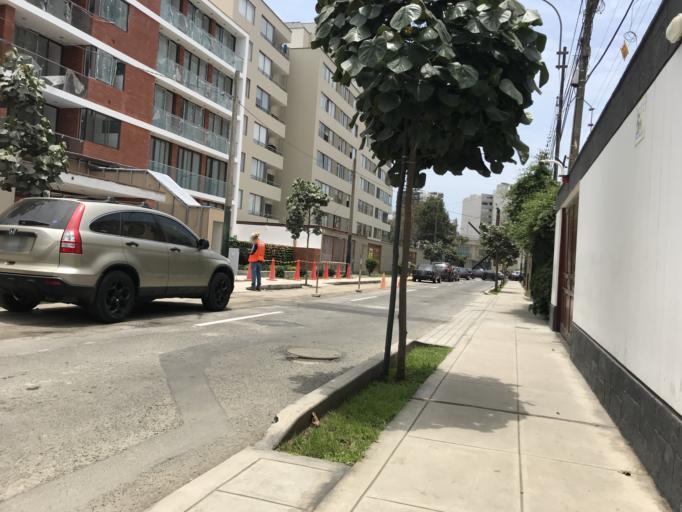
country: PE
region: Lima
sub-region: Lima
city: San Isidro
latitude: -12.0926
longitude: -77.0521
